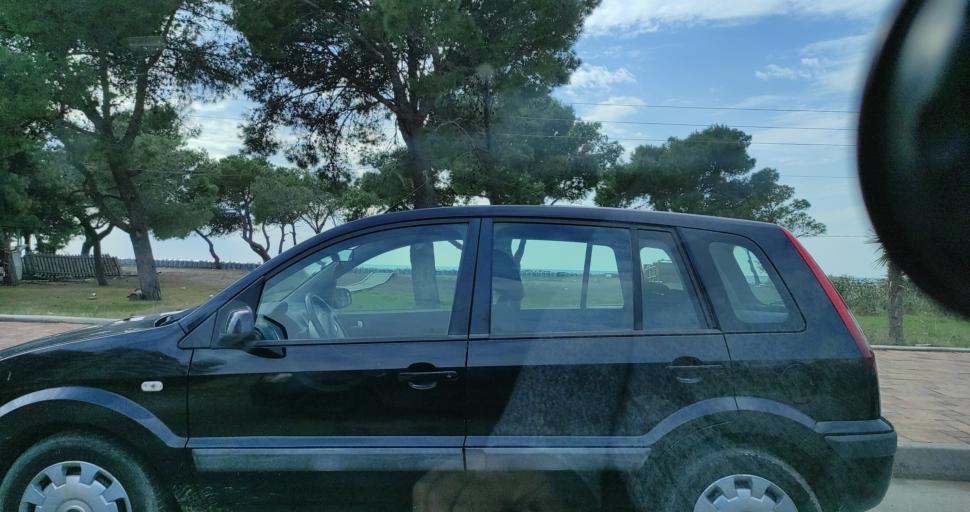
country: AL
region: Lezhe
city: Shengjin
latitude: 41.8042
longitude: 19.6002
